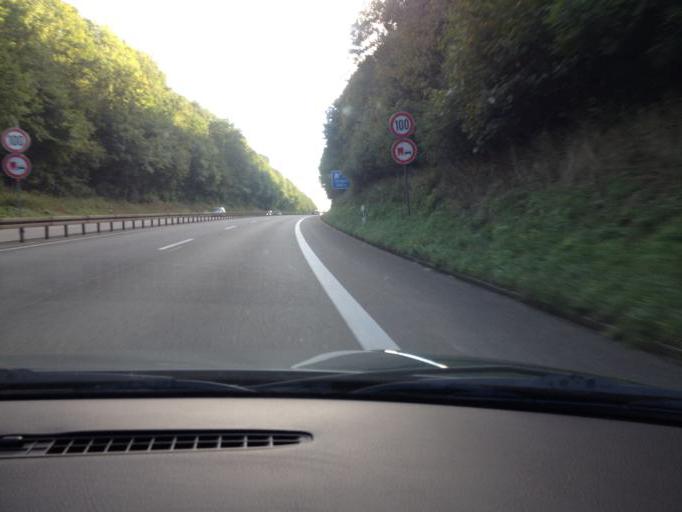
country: DE
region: Saarland
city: Illingen
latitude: 49.3908
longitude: 7.0102
